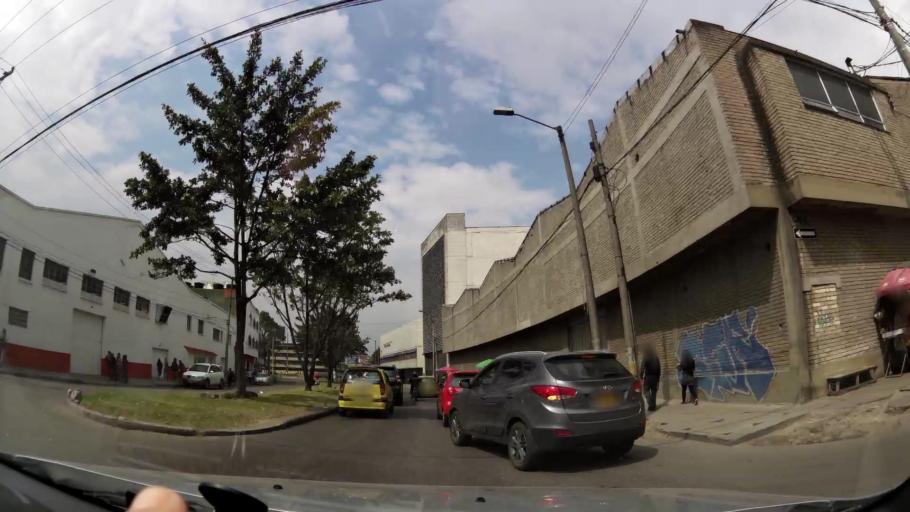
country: CO
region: Bogota D.C.
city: Bogota
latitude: 4.6249
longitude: -74.1006
